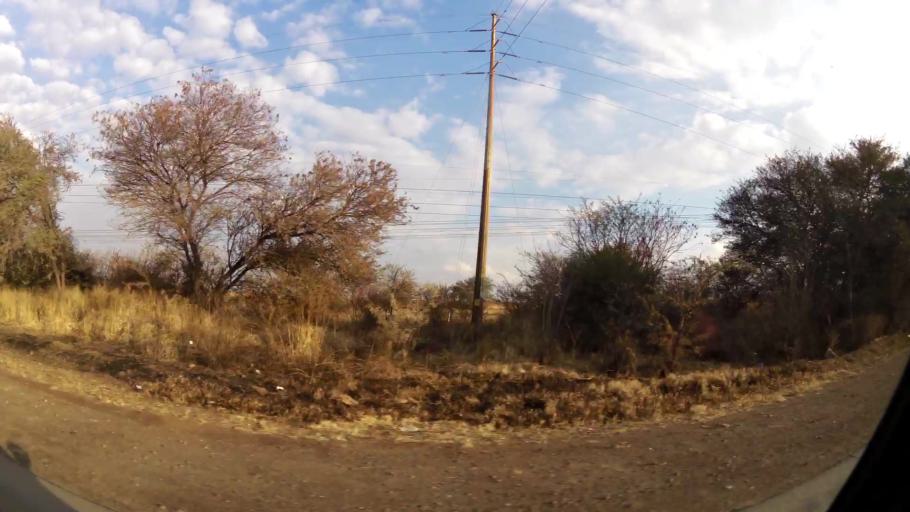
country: ZA
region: Gauteng
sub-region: Sedibeng District Municipality
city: Vereeniging
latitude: -26.6239
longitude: 27.8590
